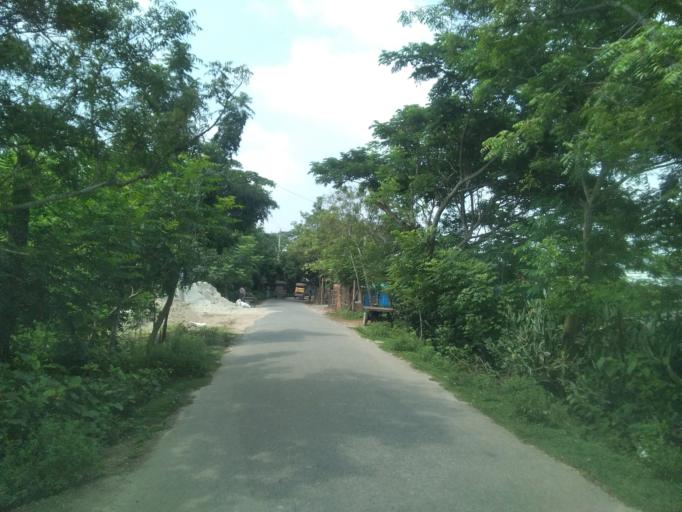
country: BD
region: Khulna
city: Phultala
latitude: 22.7006
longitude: 89.4544
